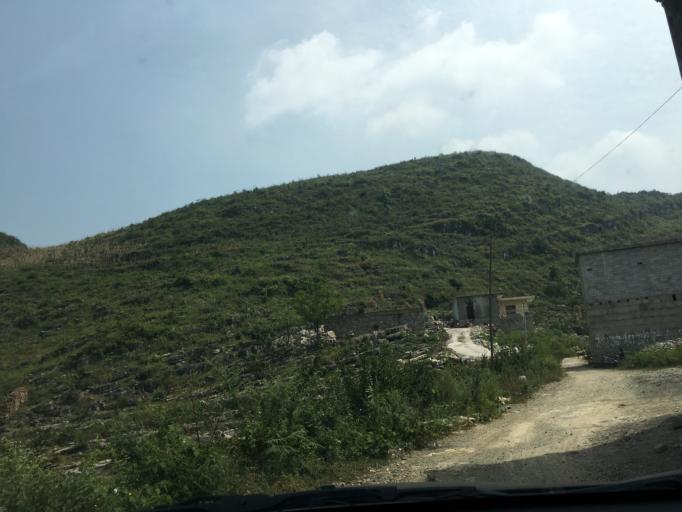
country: CN
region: Guizhou Sheng
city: Anshun
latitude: 25.5995
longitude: 105.6682
